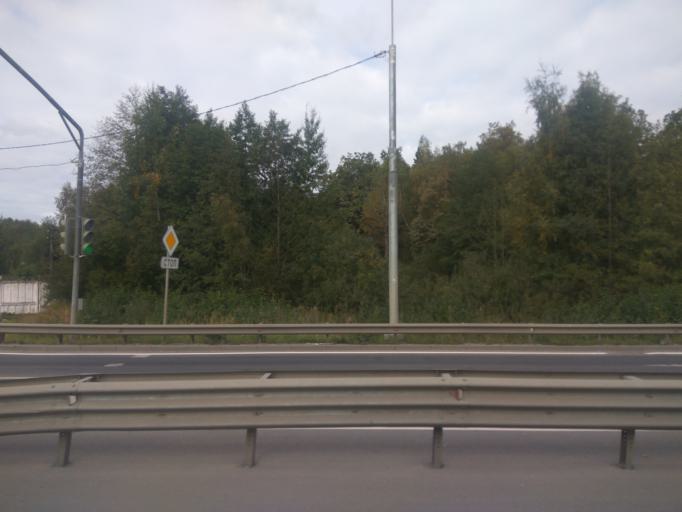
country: RU
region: Moskovskaya
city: Fryazino
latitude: 55.9409
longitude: 38.0354
